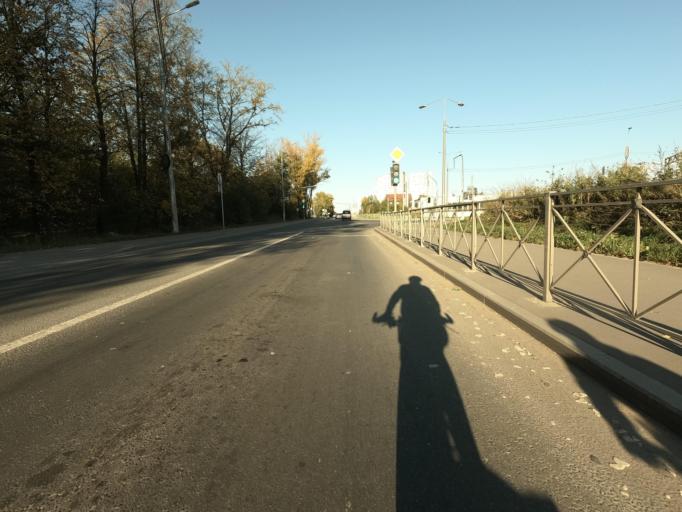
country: RU
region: St.-Petersburg
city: Pontonnyy
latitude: 59.7590
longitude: 30.6224
